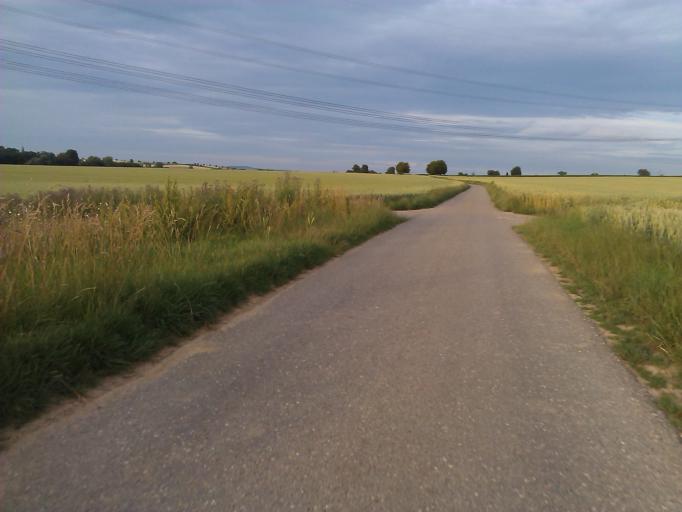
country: DE
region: Baden-Wuerttemberg
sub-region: Regierungsbezirk Stuttgart
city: Cleebronn
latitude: 49.0628
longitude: 9.0456
